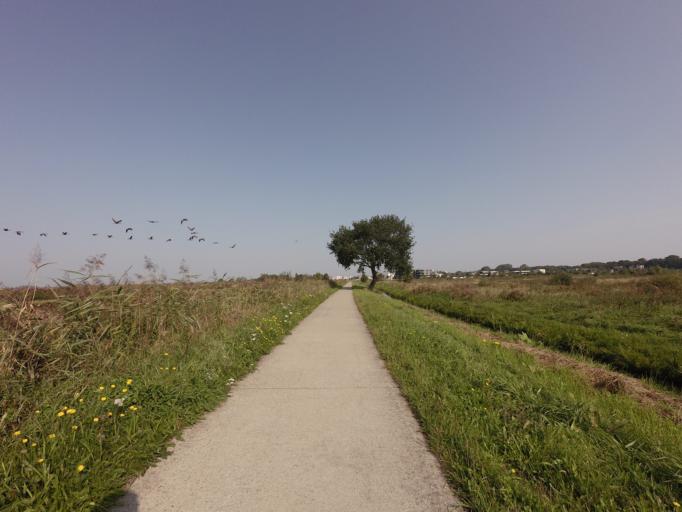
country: NL
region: Groningen
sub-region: Gemeente Groningen
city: Groningen
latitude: 53.1692
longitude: 6.5410
